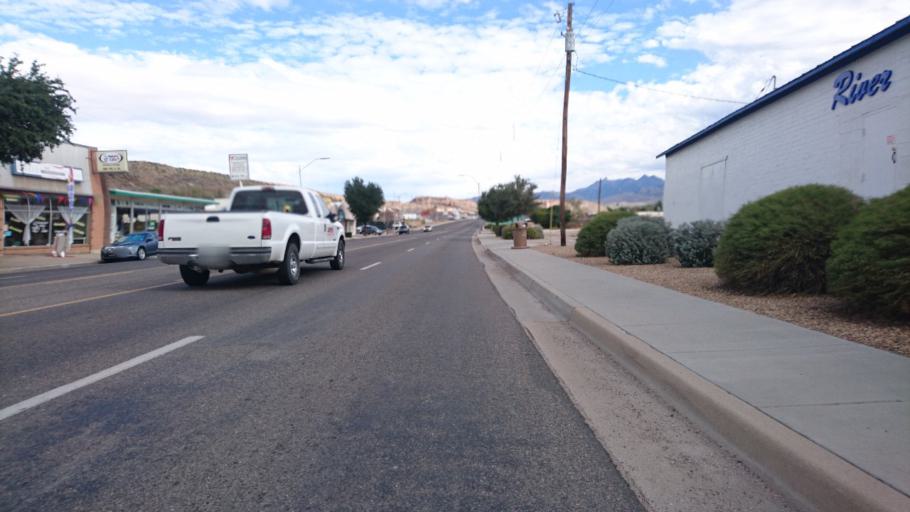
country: US
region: Arizona
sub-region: Mohave County
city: Kingman
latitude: 35.1883
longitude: -114.0508
